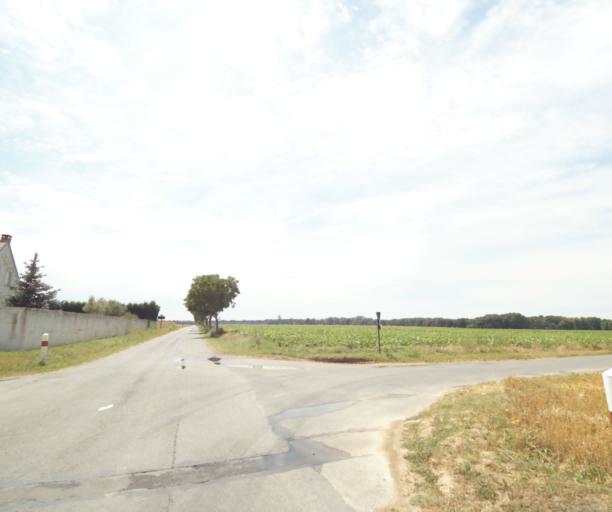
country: FR
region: Ile-de-France
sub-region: Departement de Seine-et-Marne
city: Arbonne-la-Foret
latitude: 48.4366
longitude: 2.5615
